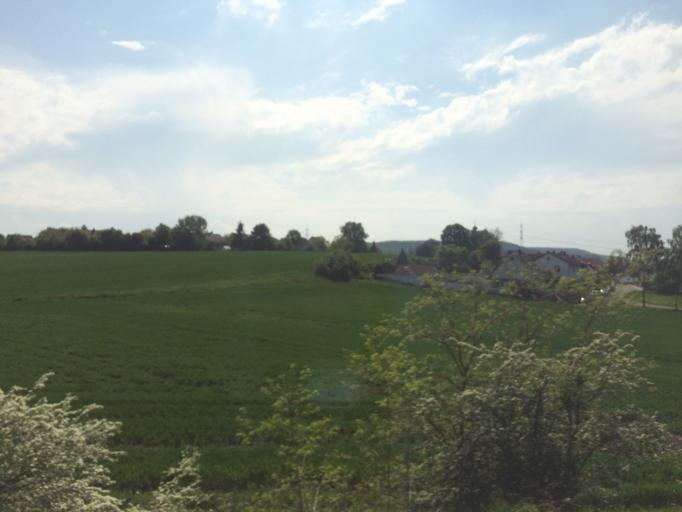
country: DE
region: Bavaria
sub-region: Regierungsbezirk Mittelfranken
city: Langenfeld
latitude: 49.6145
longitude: 10.5194
